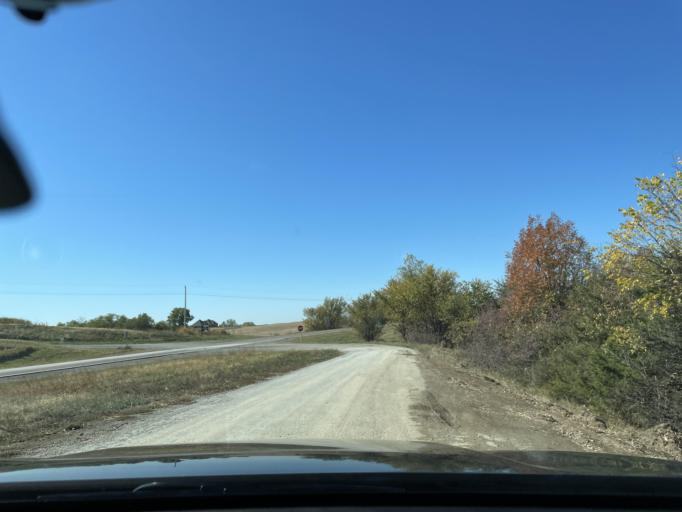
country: US
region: Missouri
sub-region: Andrew County
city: Savannah
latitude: 39.9226
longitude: -94.8614
